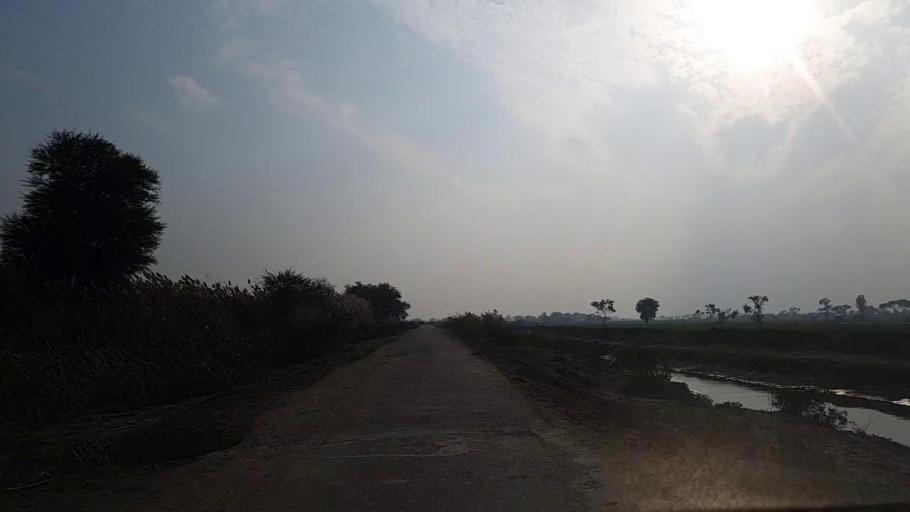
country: PK
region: Sindh
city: Jam Sahib
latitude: 26.3103
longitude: 68.5229
